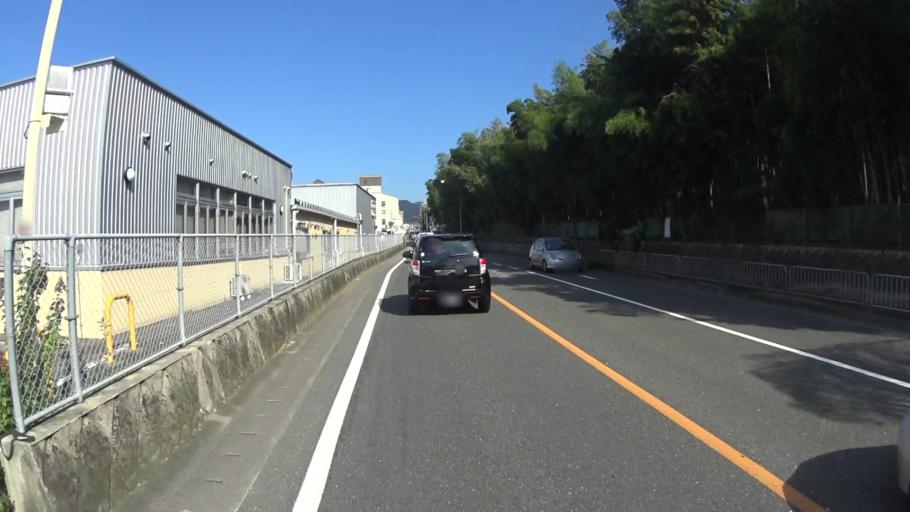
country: JP
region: Kyoto
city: Muko
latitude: 34.9648
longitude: 135.6808
